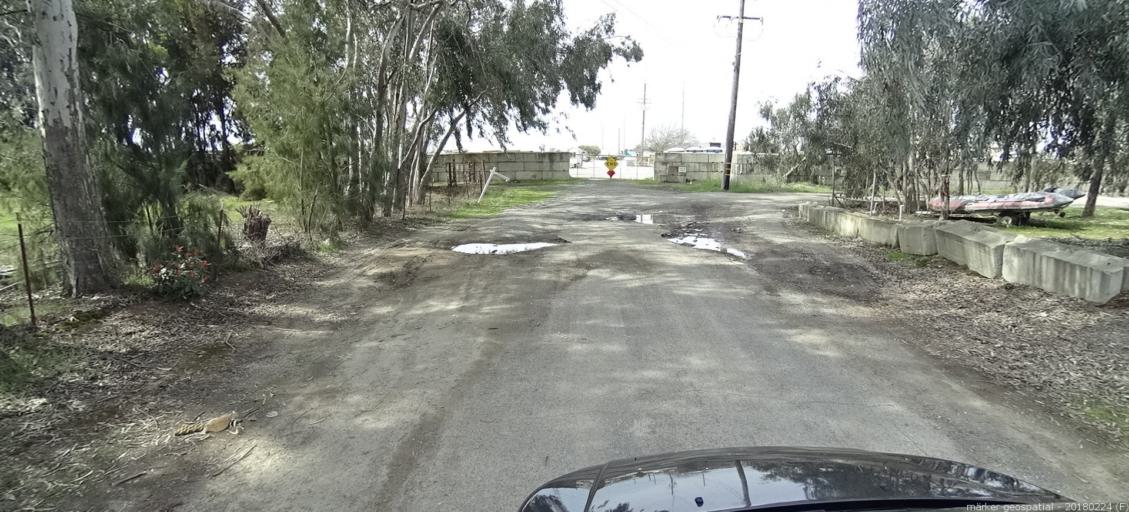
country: US
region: California
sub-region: Sacramento County
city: Elverta
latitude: 38.7100
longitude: -121.4752
